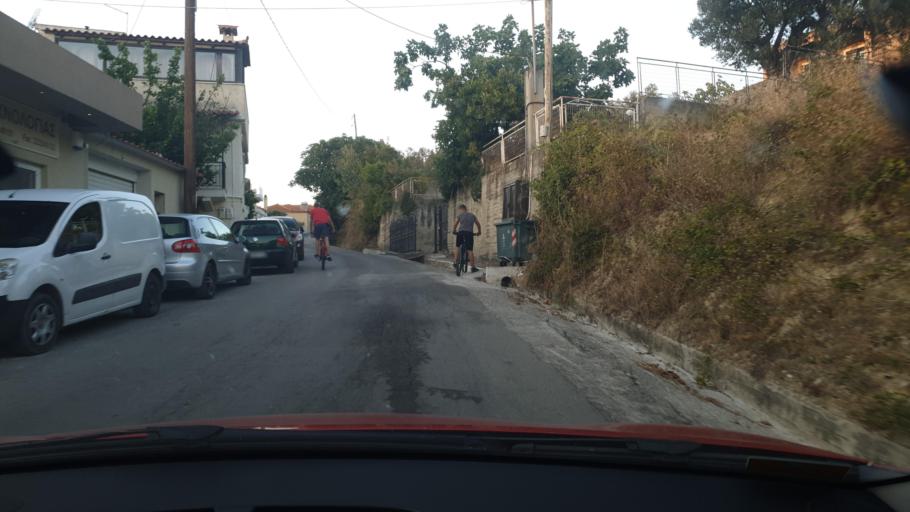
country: GR
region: Central Greece
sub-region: Nomos Evvoias
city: Oxilithos
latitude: 38.5822
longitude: 24.1108
